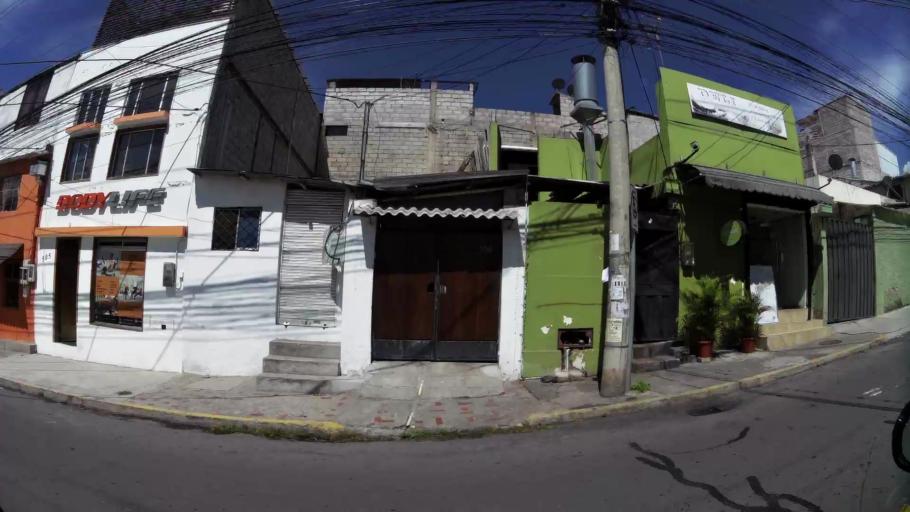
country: EC
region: Pichincha
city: Quito
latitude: -0.1985
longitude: -78.4354
